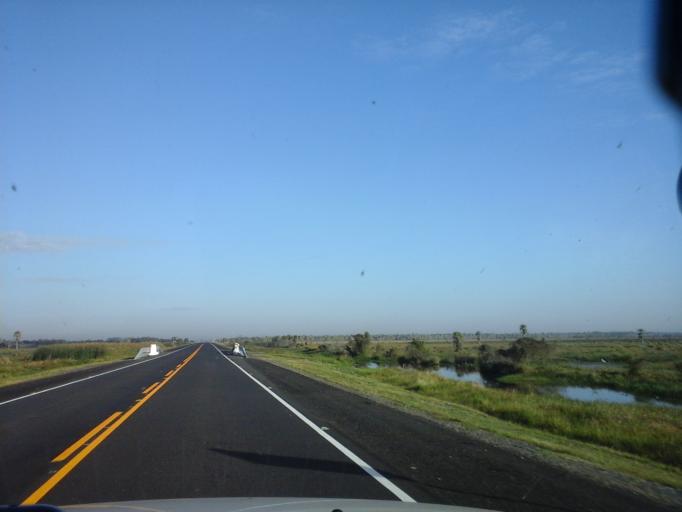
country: PY
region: Neembucu
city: Pilar
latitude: -26.8646
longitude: -57.8346
